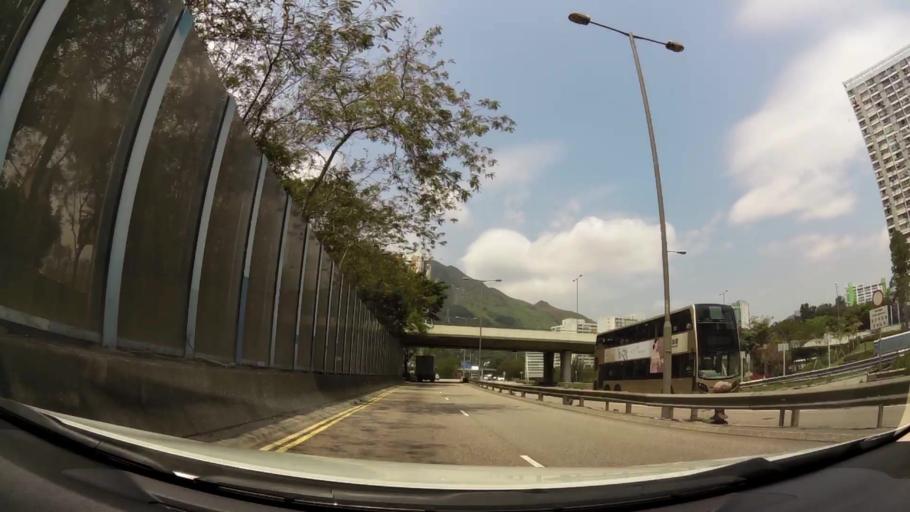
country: HK
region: Tuen Mun
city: Tuen Mun
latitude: 22.3859
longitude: 113.9715
